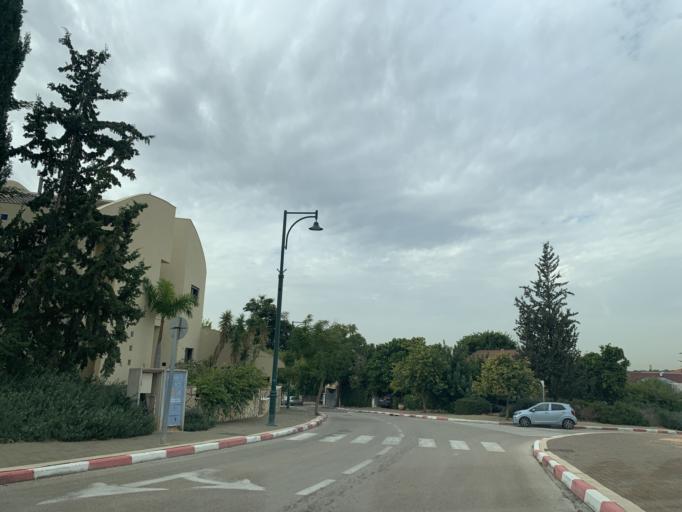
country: IL
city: Nirit
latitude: 32.1478
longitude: 34.9871
